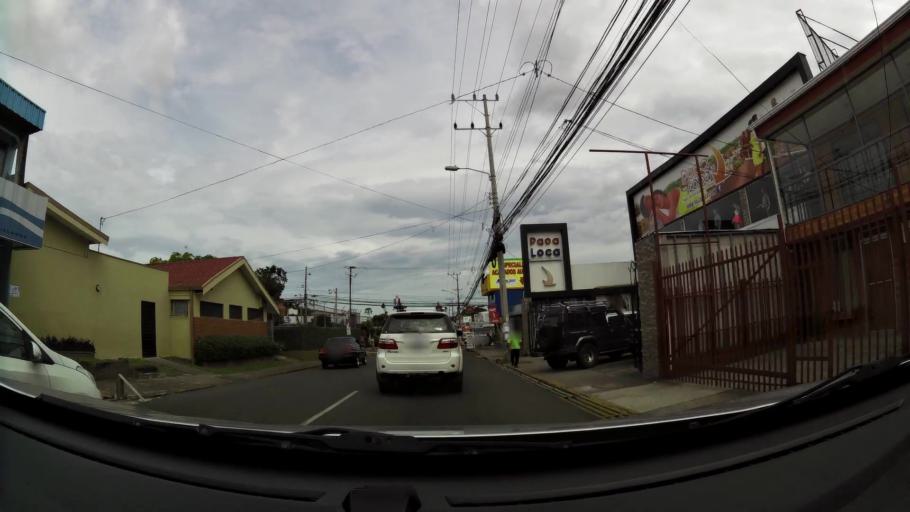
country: CR
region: San Jose
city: San Rafael Arriba
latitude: 9.8978
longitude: -84.0632
